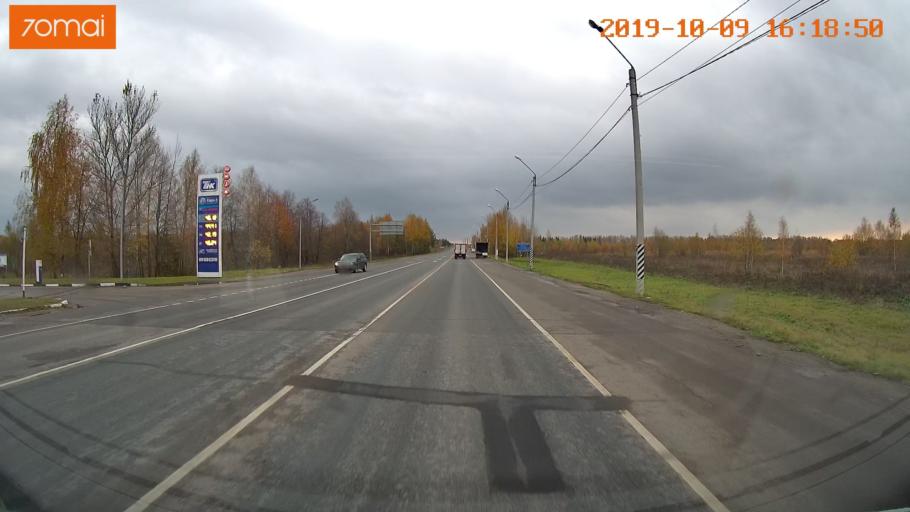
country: RU
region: Kostroma
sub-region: Kostromskoy Rayon
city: Kostroma
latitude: 57.7251
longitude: 40.8960
